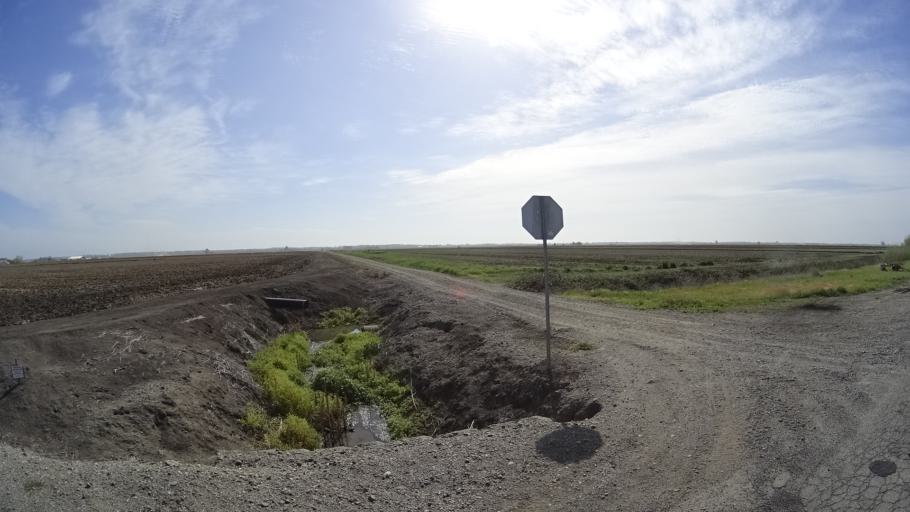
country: US
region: California
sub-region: Glenn County
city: Willows
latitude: 39.5654
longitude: -122.0464
